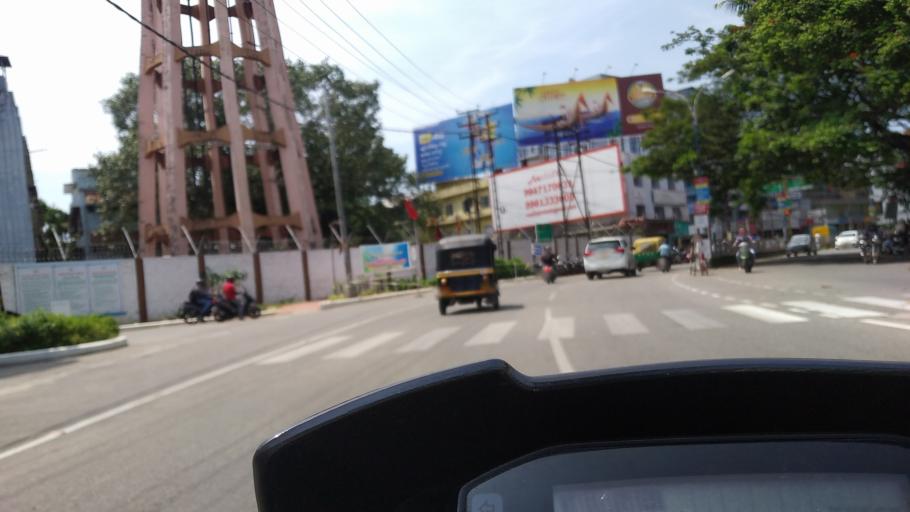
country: IN
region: Kerala
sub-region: Ernakulam
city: Cochin
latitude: 9.9571
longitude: 76.2900
